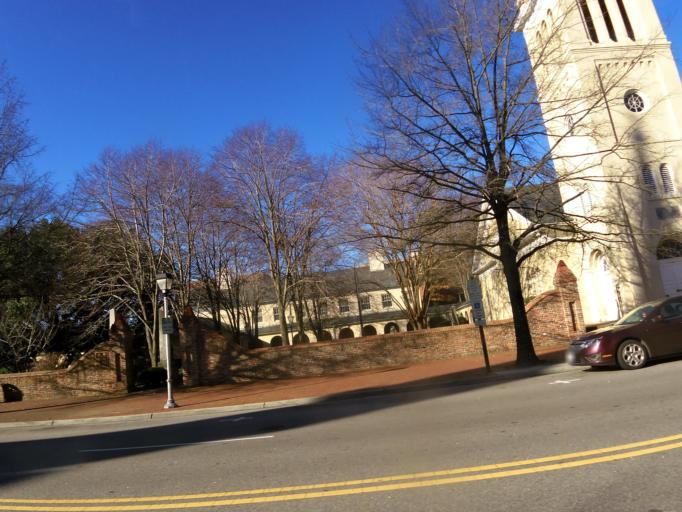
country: US
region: Virginia
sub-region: City of Portsmouth
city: Portsmouth
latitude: 36.8349
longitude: -76.3008
